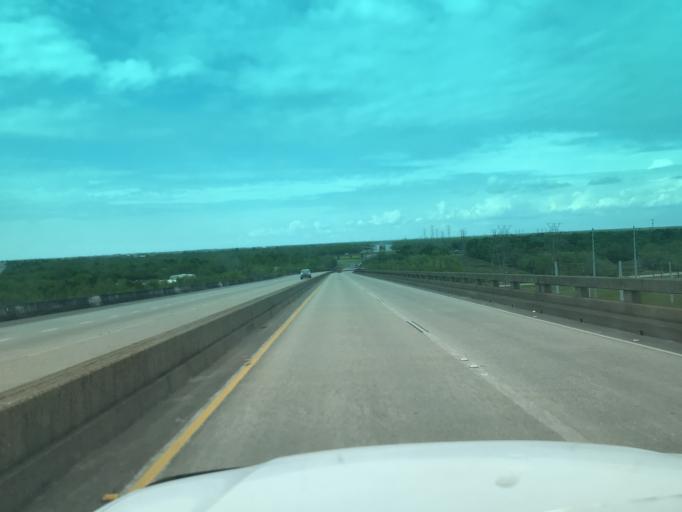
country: US
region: Louisiana
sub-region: Saint Bernard Parish
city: Chalmette
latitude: 30.0092
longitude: -89.9394
